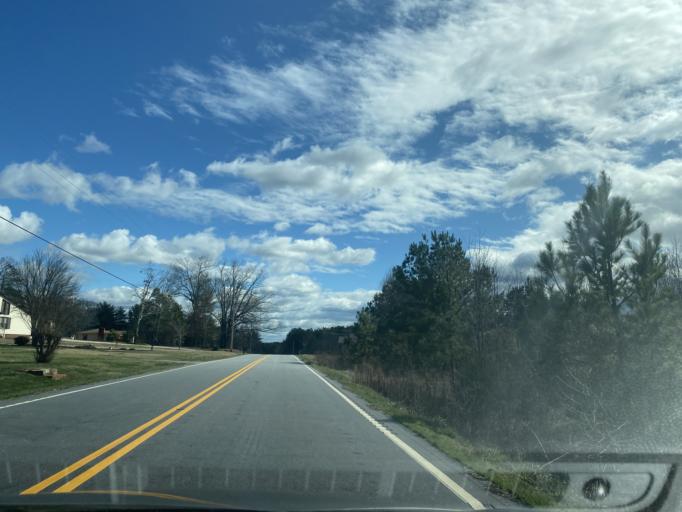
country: US
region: South Carolina
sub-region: Spartanburg County
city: Cowpens
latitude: 35.0972
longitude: -81.7536
